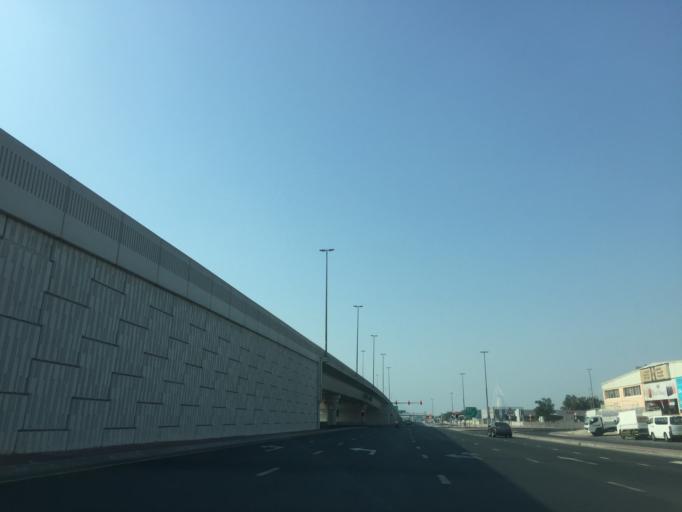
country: AE
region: Dubai
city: Dubai
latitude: 25.1103
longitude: 55.2212
